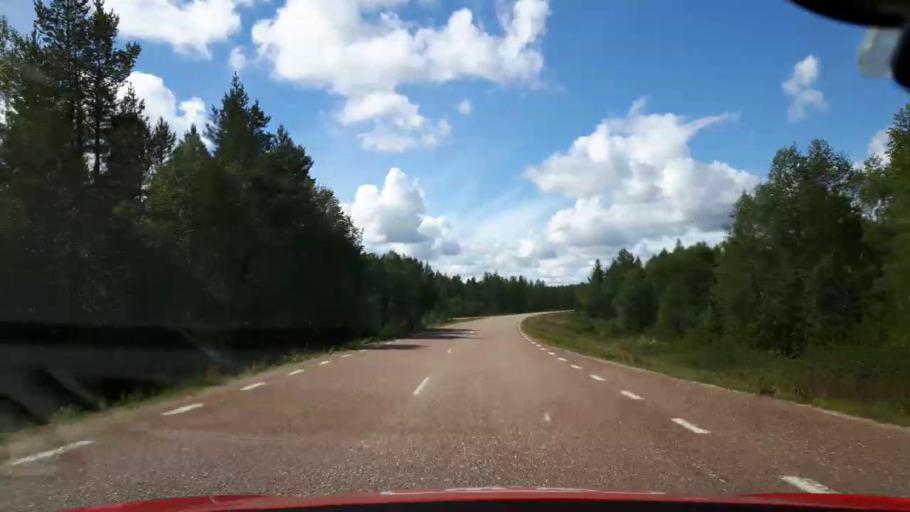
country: SE
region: Dalarna
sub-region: Alvdalens Kommun
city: AElvdalen
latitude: 61.8193
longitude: 13.5597
